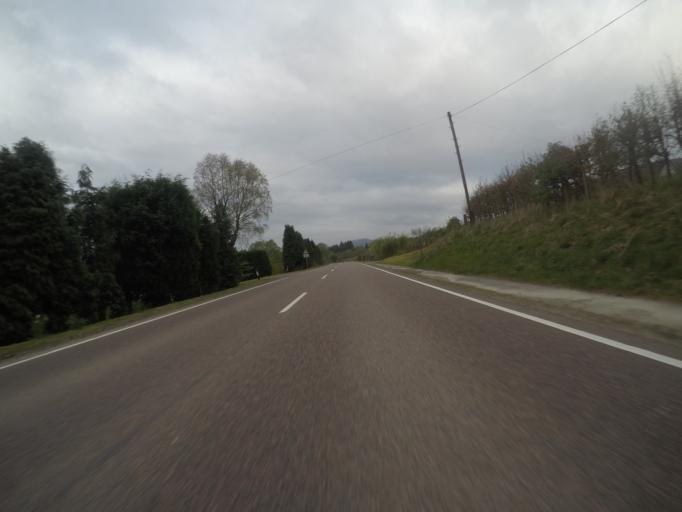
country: GB
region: Scotland
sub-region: Highland
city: Spean Bridge
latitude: 56.8905
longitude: -4.8674
